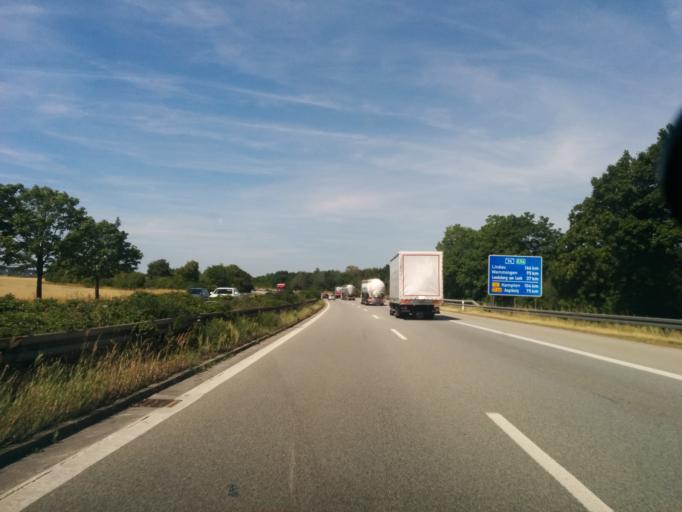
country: DE
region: Bavaria
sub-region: Upper Bavaria
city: Gilching
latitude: 48.0964
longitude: 11.3107
